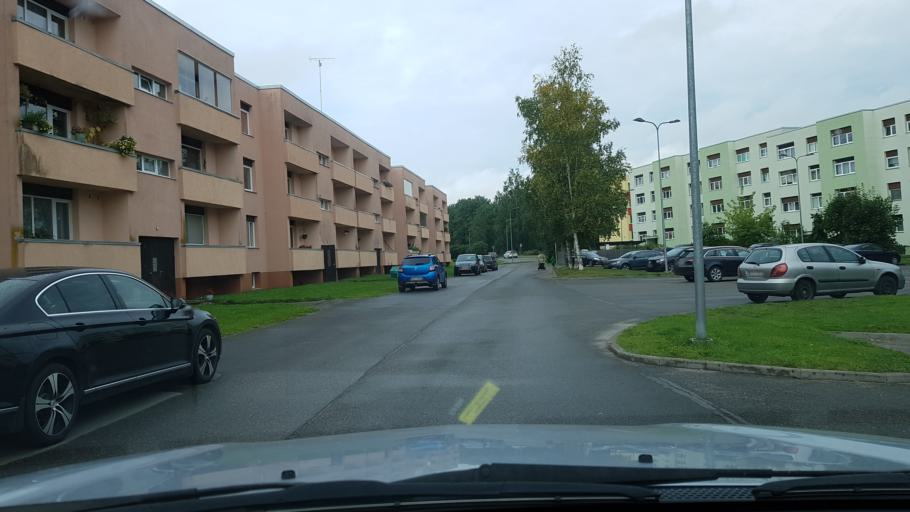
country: EE
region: Harju
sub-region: Rae vald
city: Jueri
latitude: 59.3576
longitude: 24.9180
